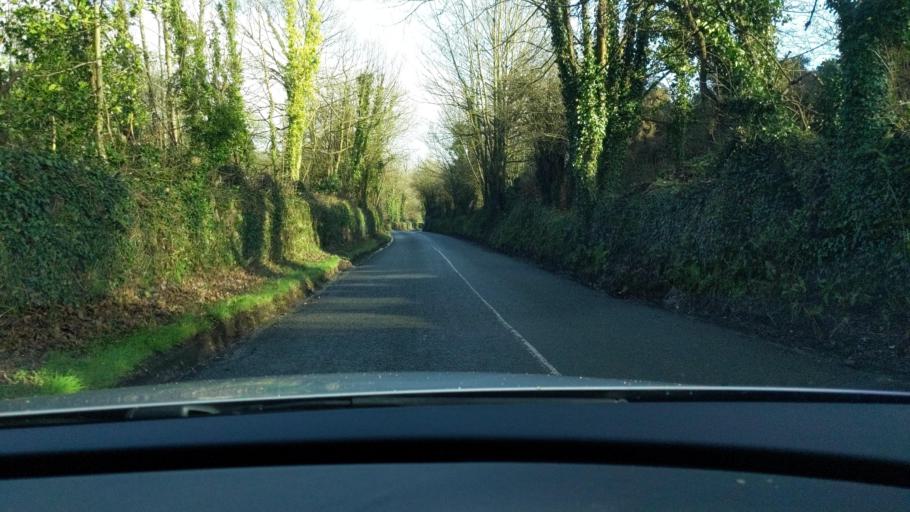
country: IE
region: Munster
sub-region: County Cork
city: Cork
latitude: 51.9264
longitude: -8.4994
